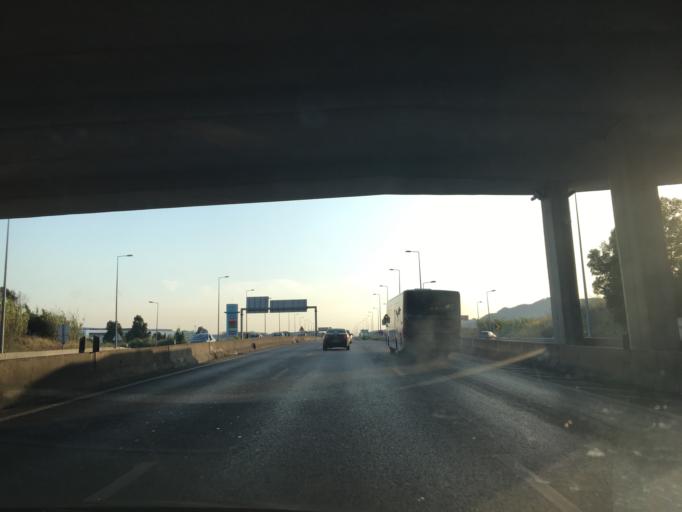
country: PT
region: Lisbon
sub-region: Sintra
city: Rio de Mouro
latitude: 38.7781
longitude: -9.3338
